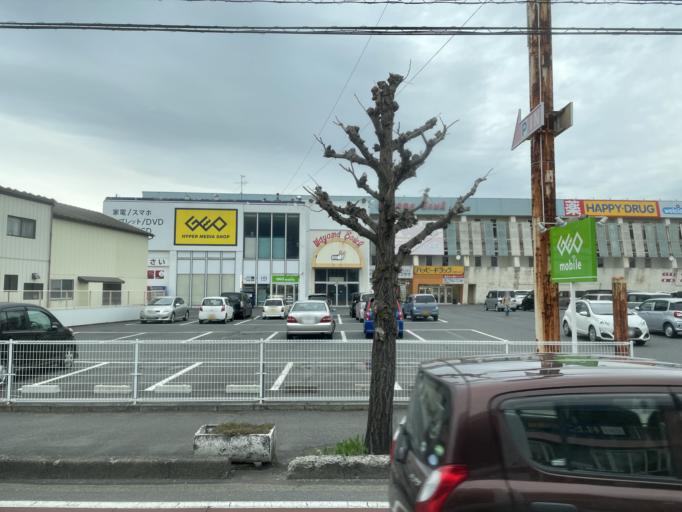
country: JP
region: Aomori
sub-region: Hachinohe Shi
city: Uchimaru
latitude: 40.5191
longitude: 141.5087
